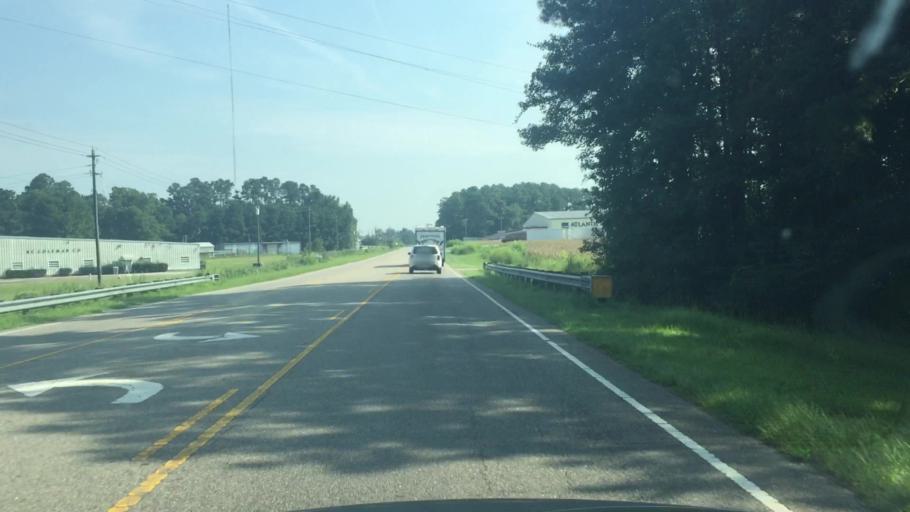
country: US
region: North Carolina
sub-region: Columbus County
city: Tabor City
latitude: 34.1488
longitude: -78.8621
